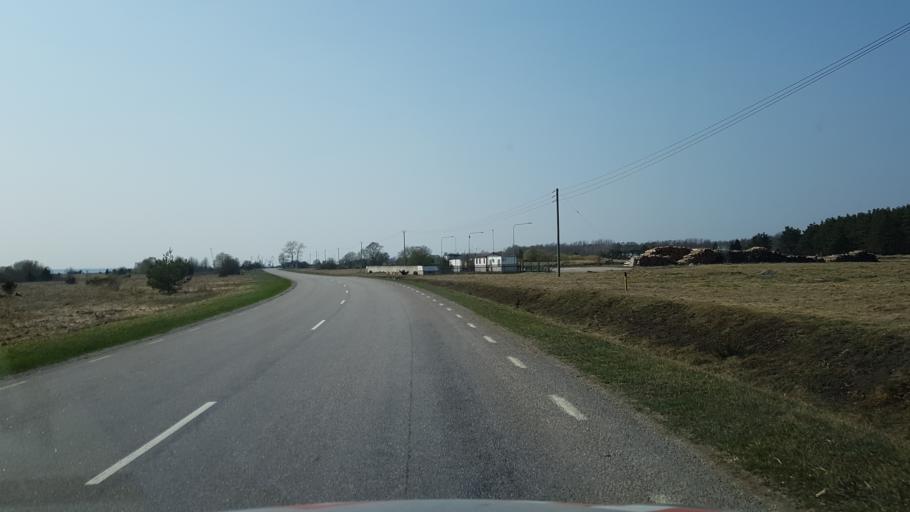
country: EE
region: Harju
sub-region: Paldiski linn
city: Paldiski
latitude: 59.3275
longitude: 24.1171
